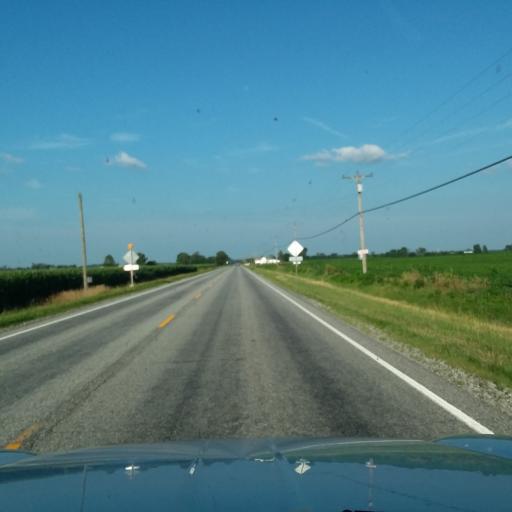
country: US
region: Indiana
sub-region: Johnson County
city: Princes Lakes
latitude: 39.4103
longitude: -86.0824
